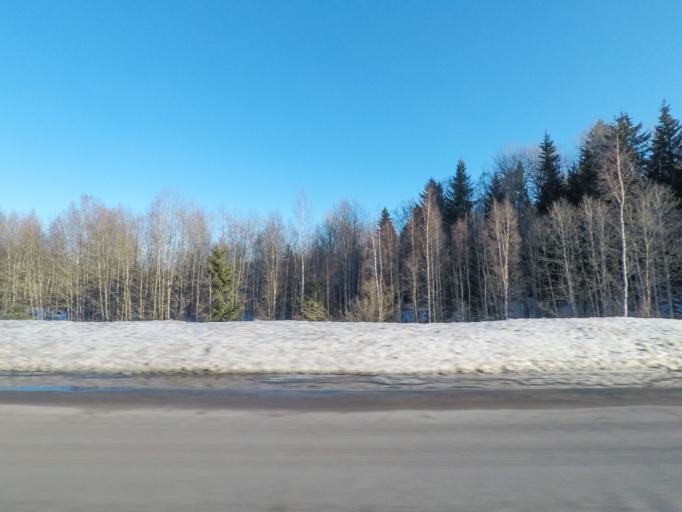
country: FI
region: Paijanne Tavastia
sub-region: Lahti
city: Lahti
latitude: 61.0011
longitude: 25.7928
